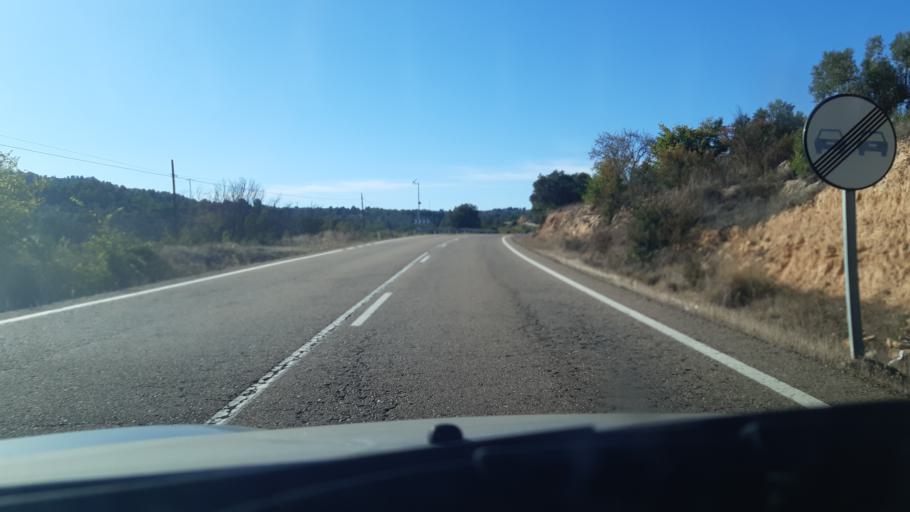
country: ES
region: Aragon
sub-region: Provincia de Teruel
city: Valjunquera
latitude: 40.9545
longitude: 0.0130
